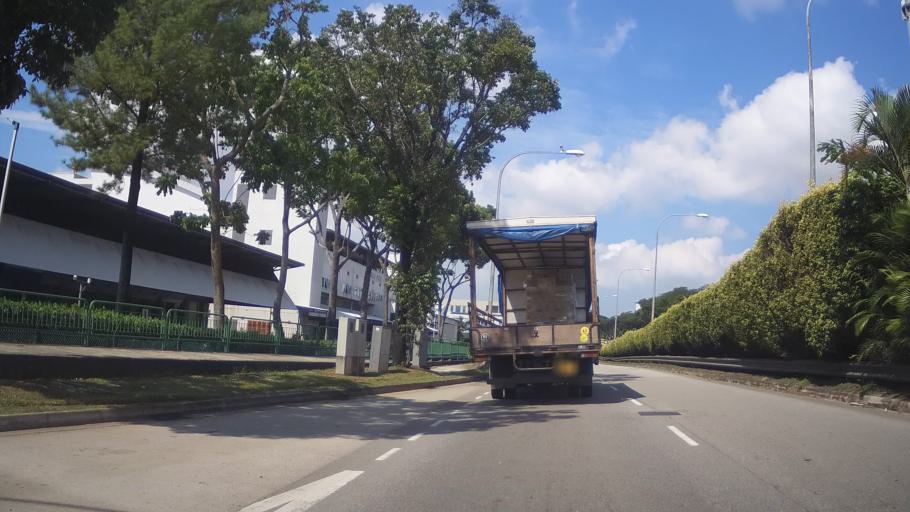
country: SG
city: Singapore
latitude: 1.3230
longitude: 103.7181
